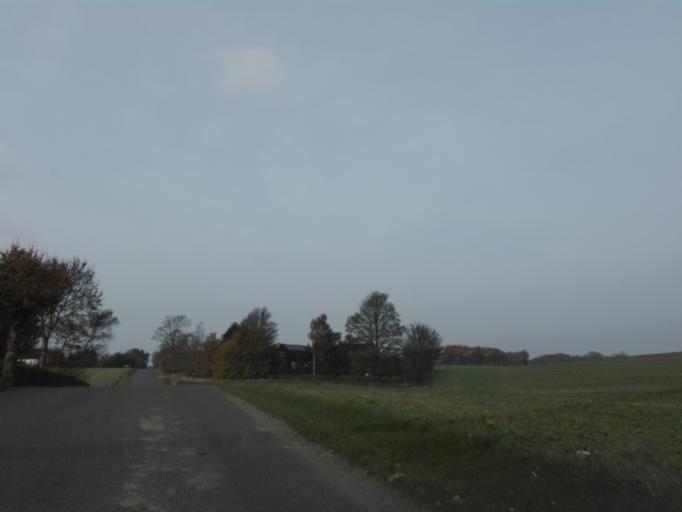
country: DK
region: Central Jutland
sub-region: Arhus Kommune
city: Solbjerg
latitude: 56.0261
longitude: 10.0684
